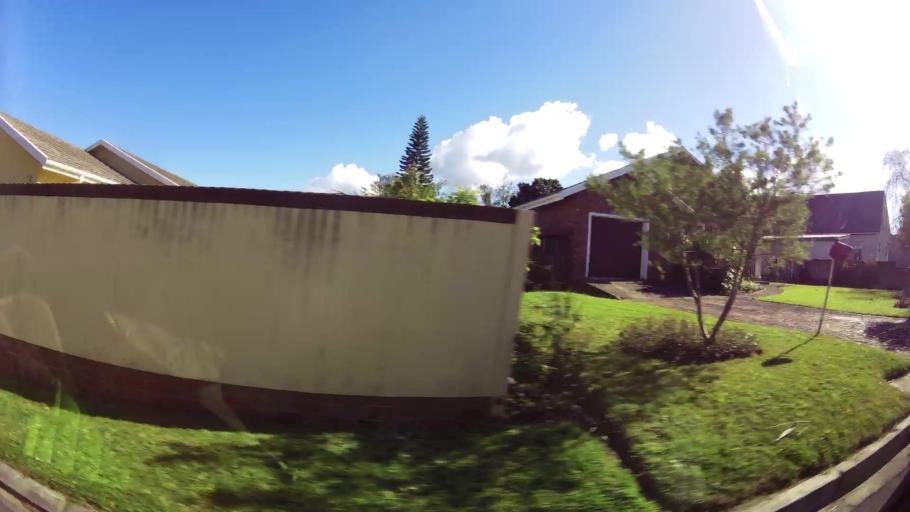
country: ZA
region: Western Cape
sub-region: Eden District Municipality
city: George
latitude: -33.9474
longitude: 22.4078
